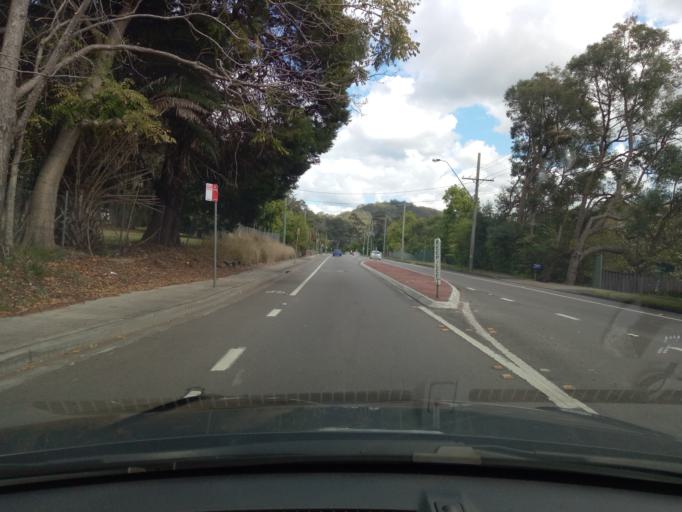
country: AU
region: New South Wales
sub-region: Gosford Shire
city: Narara
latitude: -33.4043
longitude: 151.3402
